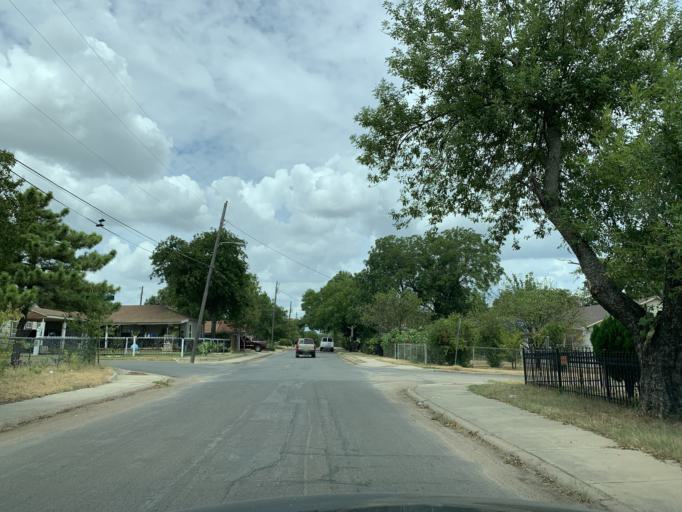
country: US
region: Texas
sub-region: Dallas County
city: Cockrell Hill
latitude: 32.7429
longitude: -96.8773
